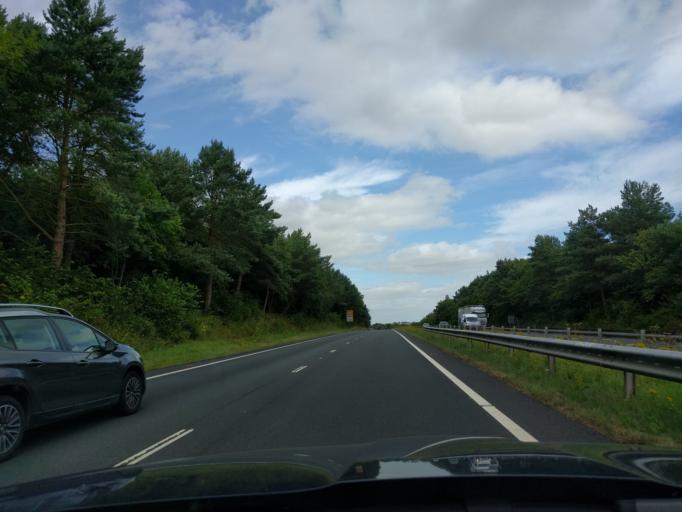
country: GB
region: England
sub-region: Northumberland
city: Felton
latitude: 55.3192
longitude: -1.7249
